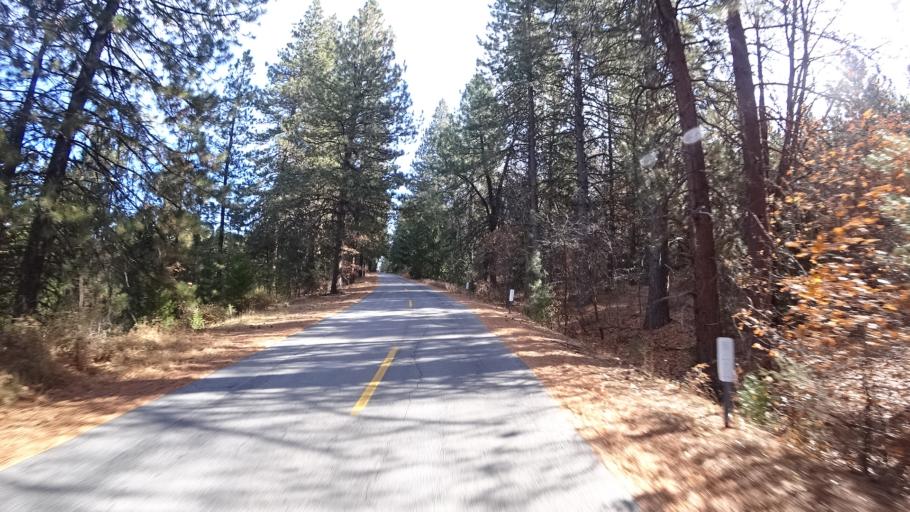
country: US
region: California
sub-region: Siskiyou County
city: Weed
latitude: 41.4309
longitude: -122.4122
